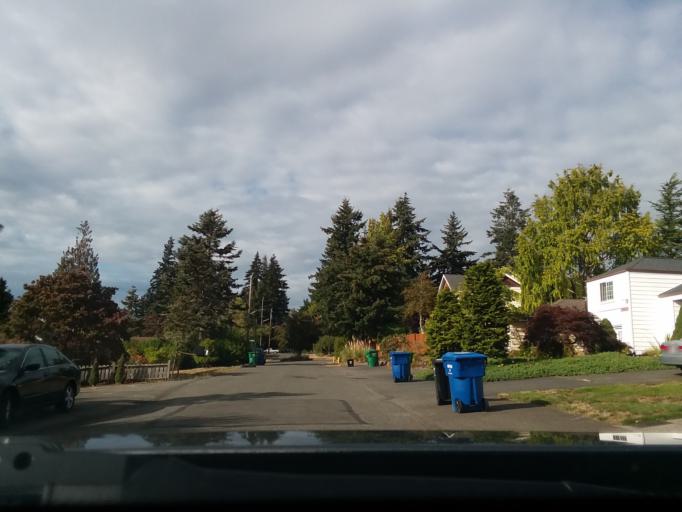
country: US
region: Washington
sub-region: King County
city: Shoreline
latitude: 47.7153
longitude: -122.3623
